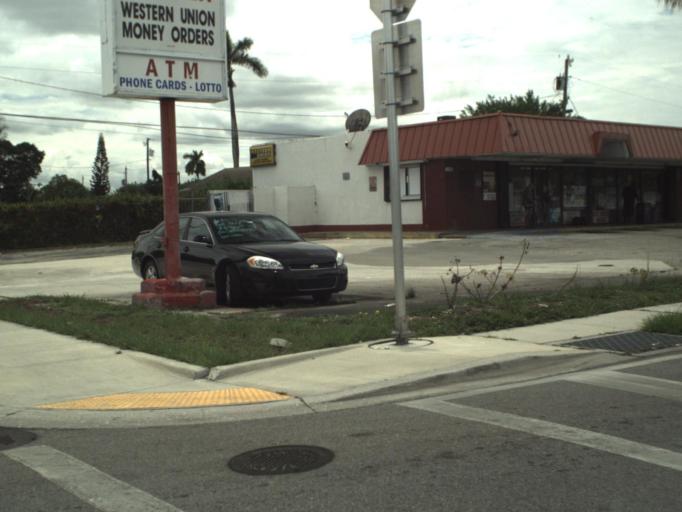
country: US
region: Florida
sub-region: Palm Beach County
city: Riviera Beach
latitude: 26.7899
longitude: -80.0545
